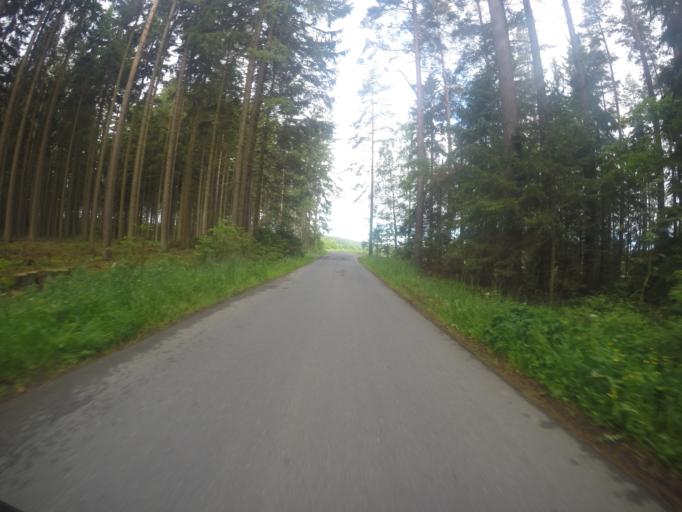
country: DE
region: Bavaria
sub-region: Upper Franconia
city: Schonwald
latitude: 50.2111
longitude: 12.1118
